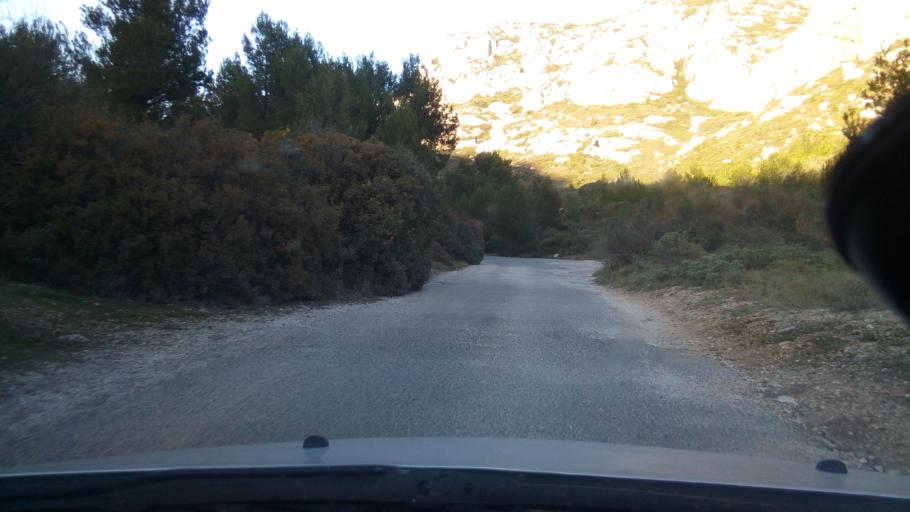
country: FR
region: Provence-Alpes-Cote d'Azur
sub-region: Departement des Bouches-du-Rhone
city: Marseille 09
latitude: 43.2196
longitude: 5.4079
